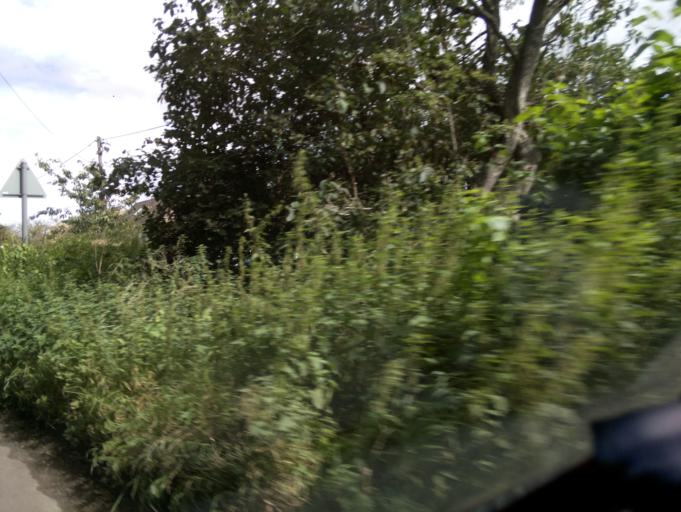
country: GB
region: England
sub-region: Wiltshire
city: Colerne
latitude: 51.4521
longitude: -2.2571
